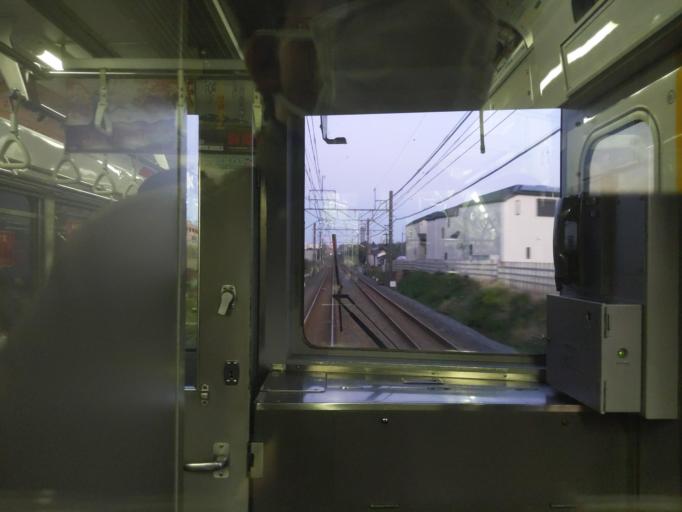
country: JP
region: Chiba
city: Kashiwa
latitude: 35.8627
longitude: 139.9500
